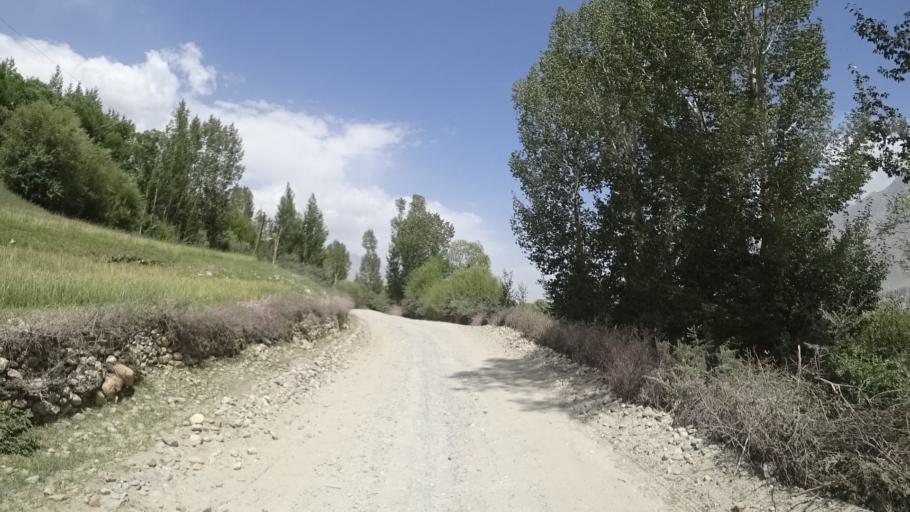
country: AF
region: Badakhshan
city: Khandud
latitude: 36.9400
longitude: 72.2229
